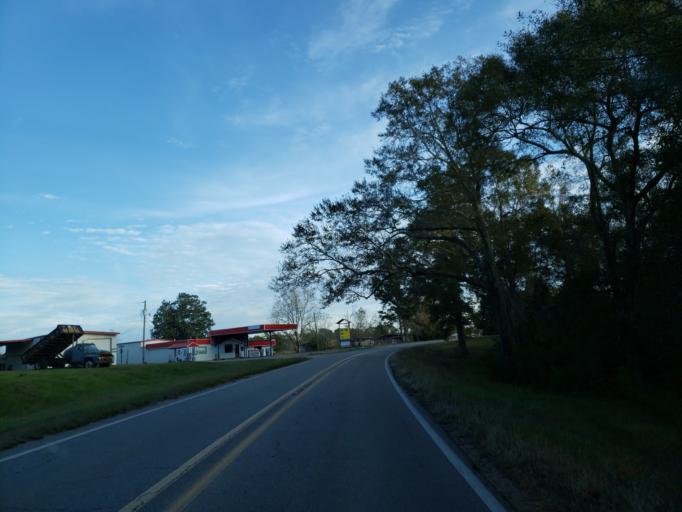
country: US
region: Mississippi
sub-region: Lamar County
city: Purvis
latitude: 31.1726
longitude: -89.4283
